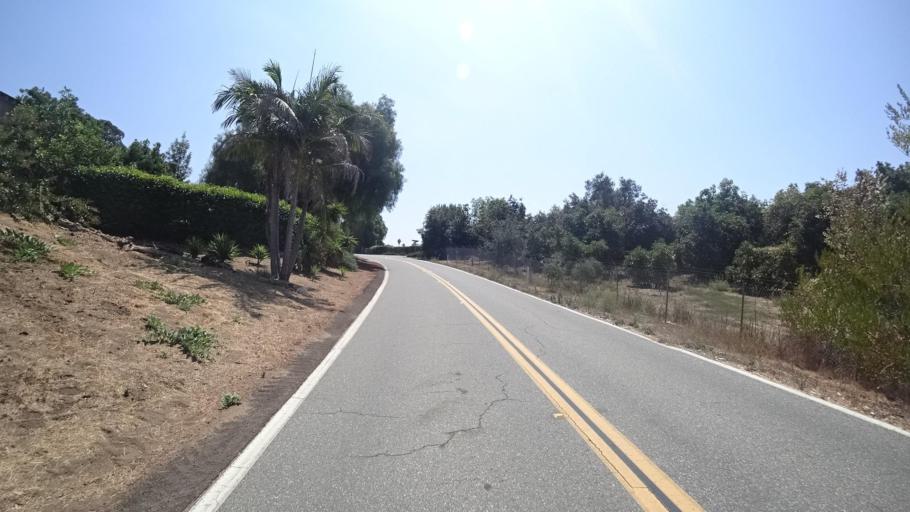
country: US
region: California
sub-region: San Diego County
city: Fallbrook
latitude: 33.3377
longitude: -117.2286
